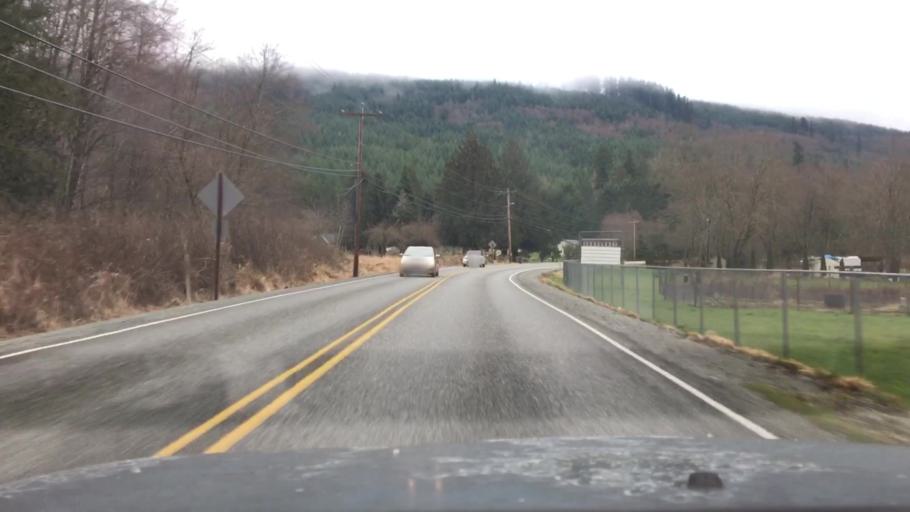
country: US
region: Washington
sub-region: Whatcom County
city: Sudden Valley
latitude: 48.6390
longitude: -122.3130
